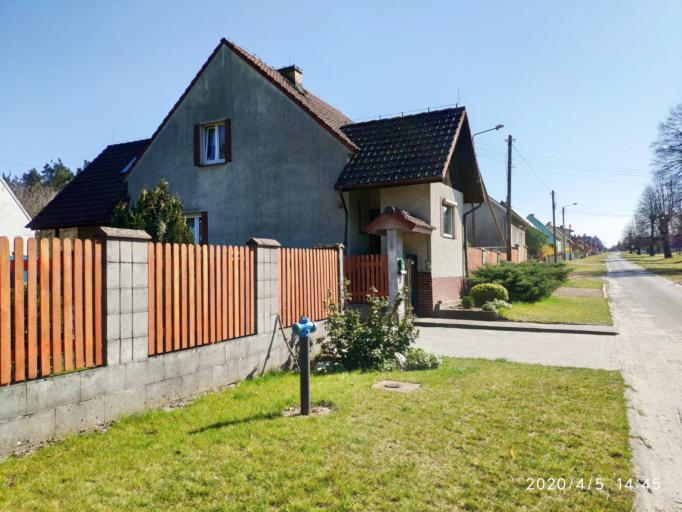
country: PL
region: Lubusz
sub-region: Powiat krosnienski
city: Dabie
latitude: 52.0329
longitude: 15.2494
